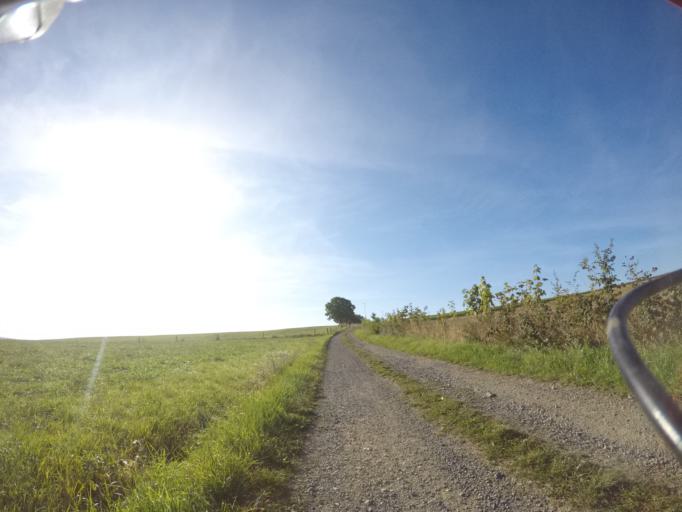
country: BE
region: Wallonia
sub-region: Province du Luxembourg
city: Fauvillers
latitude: 49.9140
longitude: 5.6594
